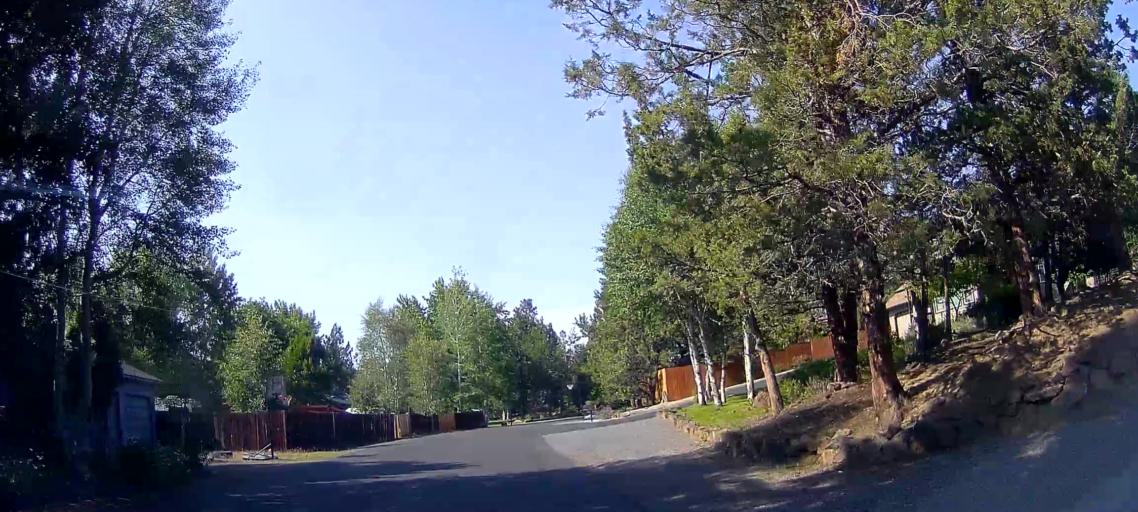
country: US
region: Oregon
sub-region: Deschutes County
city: Bend
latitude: 44.0345
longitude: -121.2820
